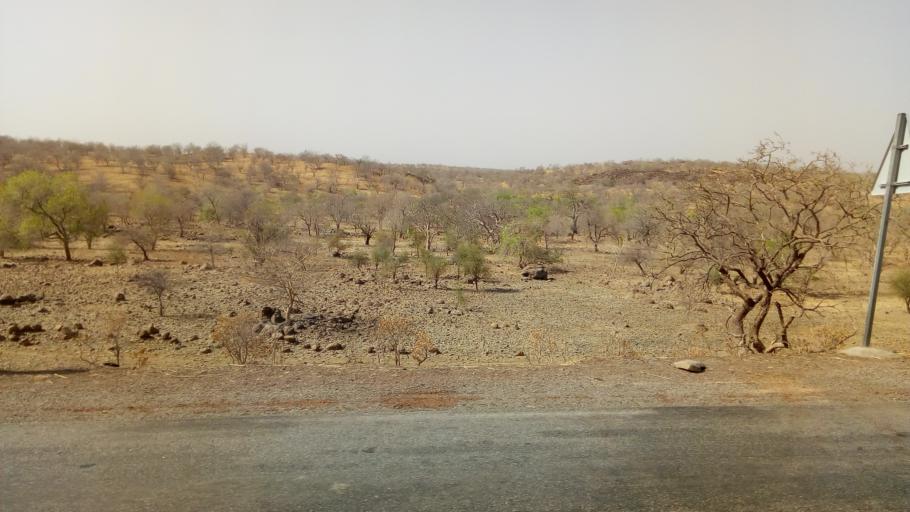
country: ML
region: Kayes
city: Yelimane
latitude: 14.6453
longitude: -10.6612
